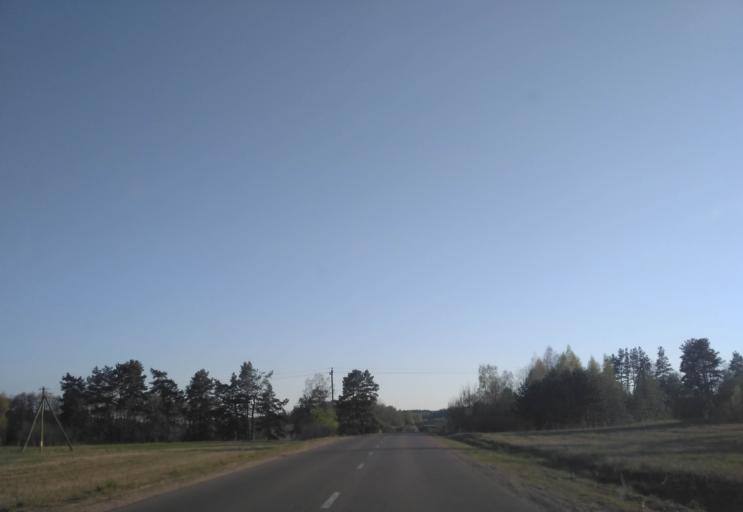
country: BY
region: Minsk
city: Radashkovichy
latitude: 54.1447
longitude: 27.2118
